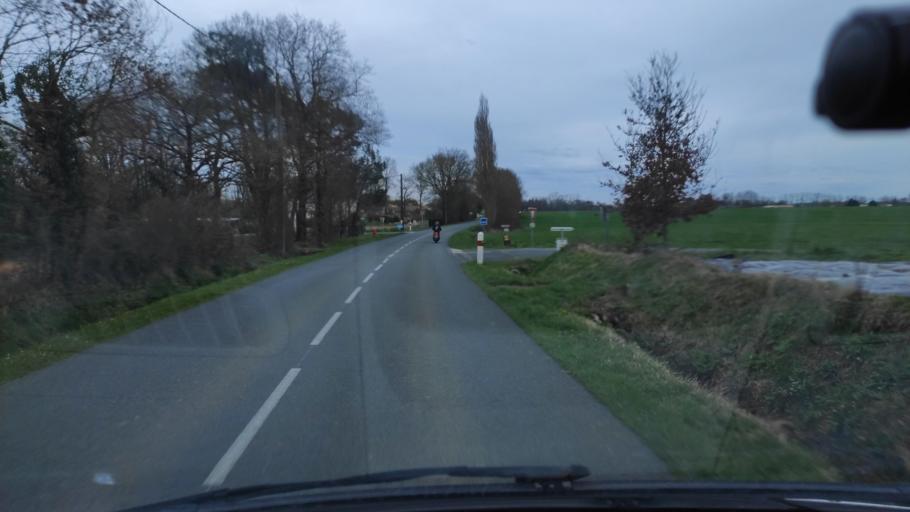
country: FR
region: Pays de la Loire
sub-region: Departement de la Vendee
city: Saint-Andre-Treize-Voies
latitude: 46.9021
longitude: -1.4355
